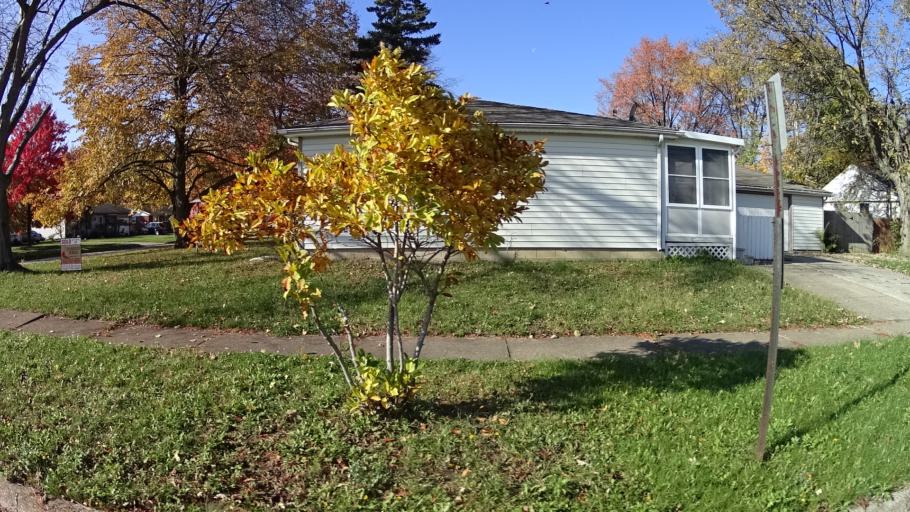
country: US
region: Ohio
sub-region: Lorain County
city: Lorain
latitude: 41.4738
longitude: -82.1439
